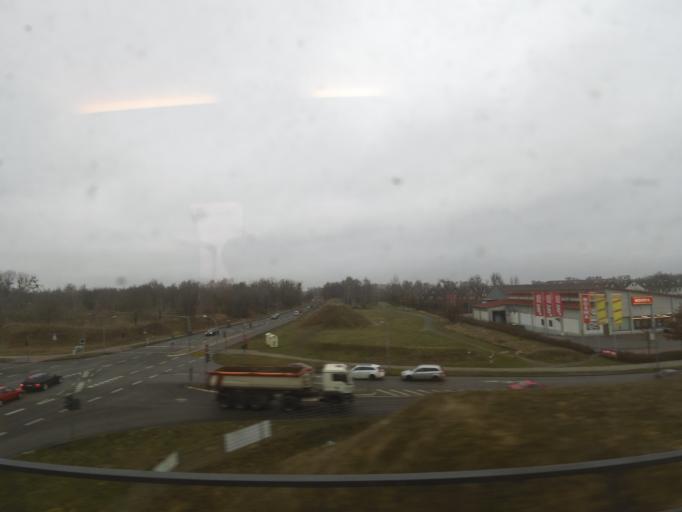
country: DE
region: Brandenburg
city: Falkensee
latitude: 52.5514
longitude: 13.1213
